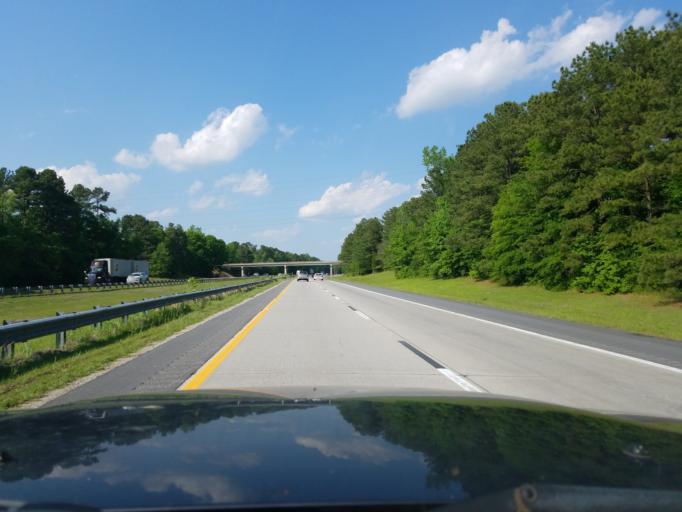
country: US
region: North Carolina
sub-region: Granville County
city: Creedmoor
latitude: 36.1697
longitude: -78.7068
